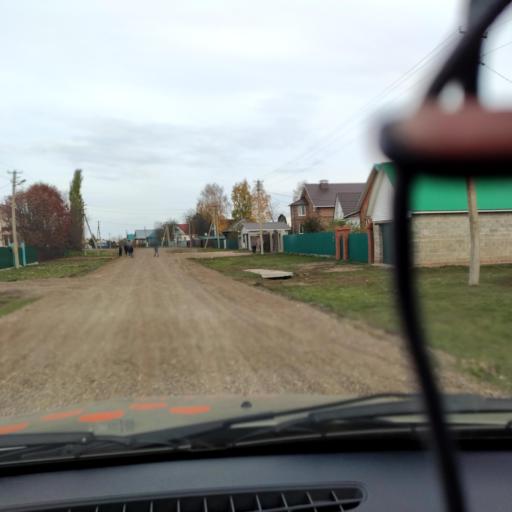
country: RU
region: Bashkortostan
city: Kabakovo
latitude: 54.5263
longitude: 56.0272
